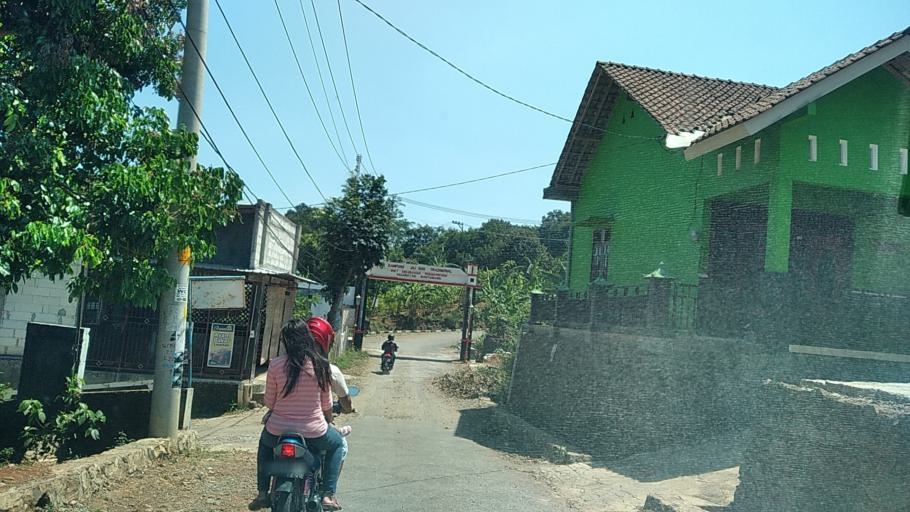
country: ID
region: Central Java
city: Ungaran
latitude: -7.0996
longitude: 110.4129
